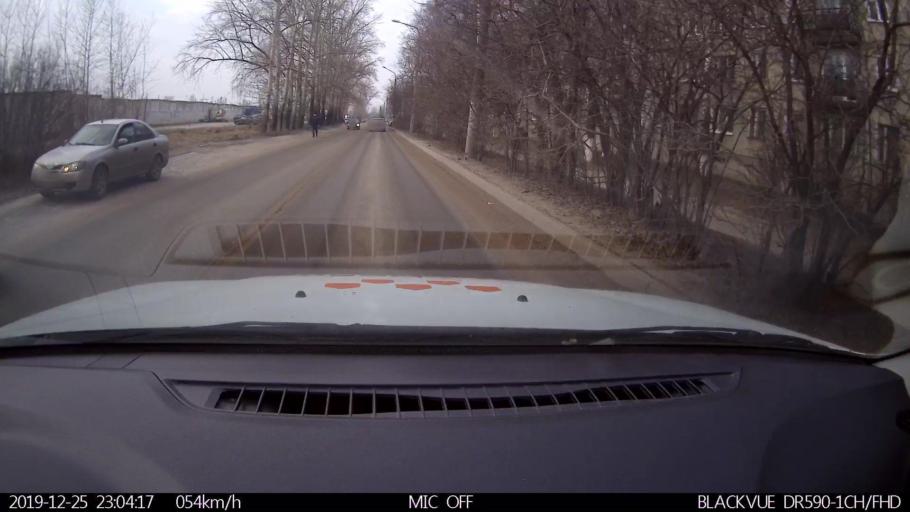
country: RU
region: Nizjnij Novgorod
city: Gorbatovka
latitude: 56.3573
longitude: 43.8119
